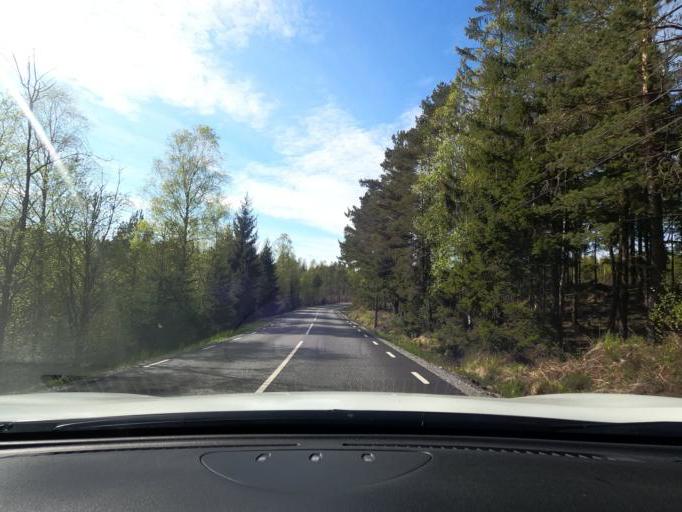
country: SE
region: Vaestra Goetaland
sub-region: Harryda Kommun
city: Landvetter
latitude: 57.6385
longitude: 12.2573
